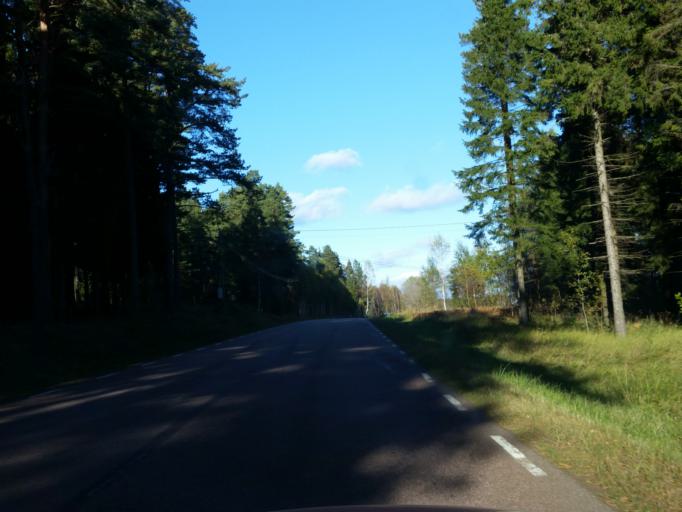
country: AX
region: Mariehamns stad
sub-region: Mariehamn
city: Mariehamn
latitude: 60.1437
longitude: 19.8608
